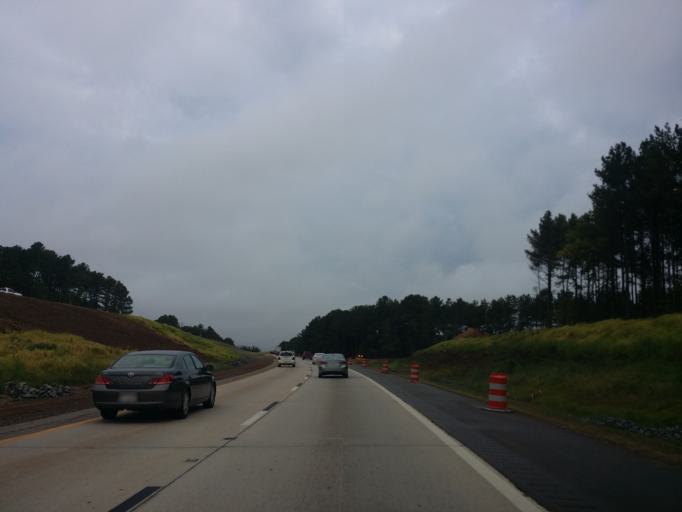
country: US
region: North Carolina
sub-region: Durham County
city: Durham
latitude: 35.9671
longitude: -78.8661
